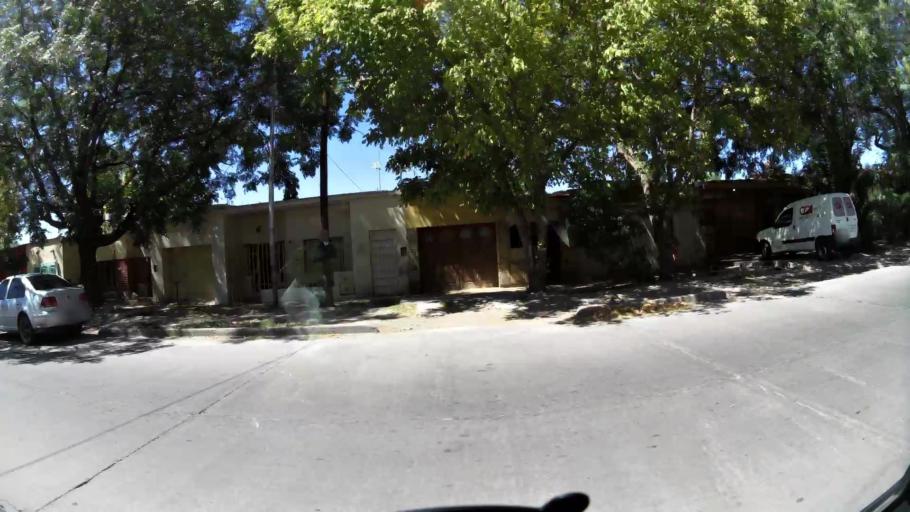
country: AR
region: Mendoza
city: Las Heras
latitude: -32.8473
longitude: -68.8467
